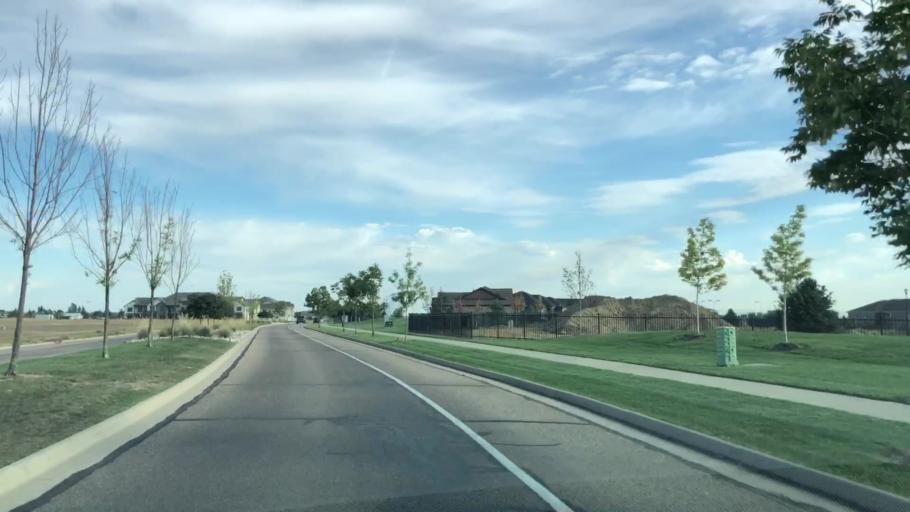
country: US
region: Colorado
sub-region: Weld County
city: Windsor
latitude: 40.4532
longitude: -104.9766
